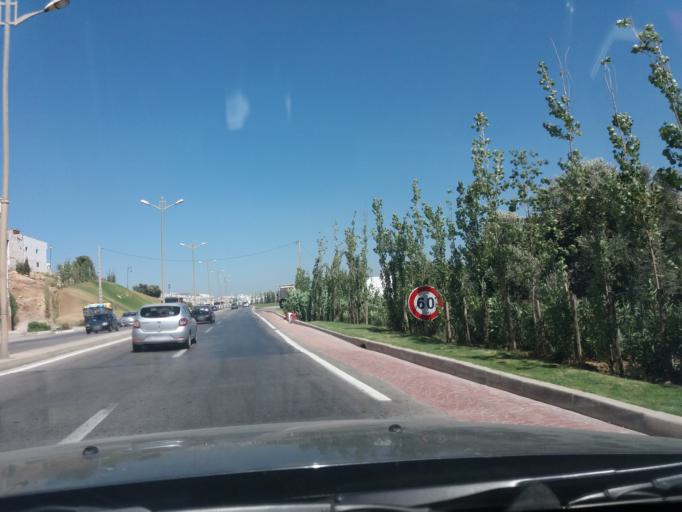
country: MA
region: Tanger-Tetouan
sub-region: Tetouan
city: Saddina
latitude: 35.5627
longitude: -5.4302
